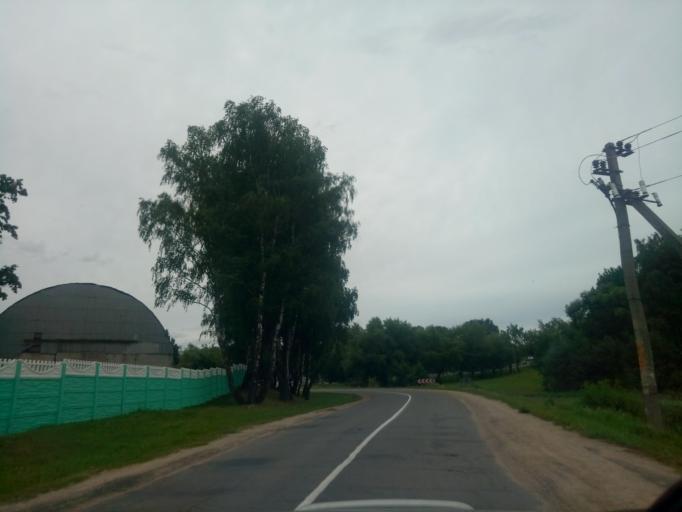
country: BY
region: Minsk
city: Zhdanovichy
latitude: 53.9233
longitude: 27.3889
